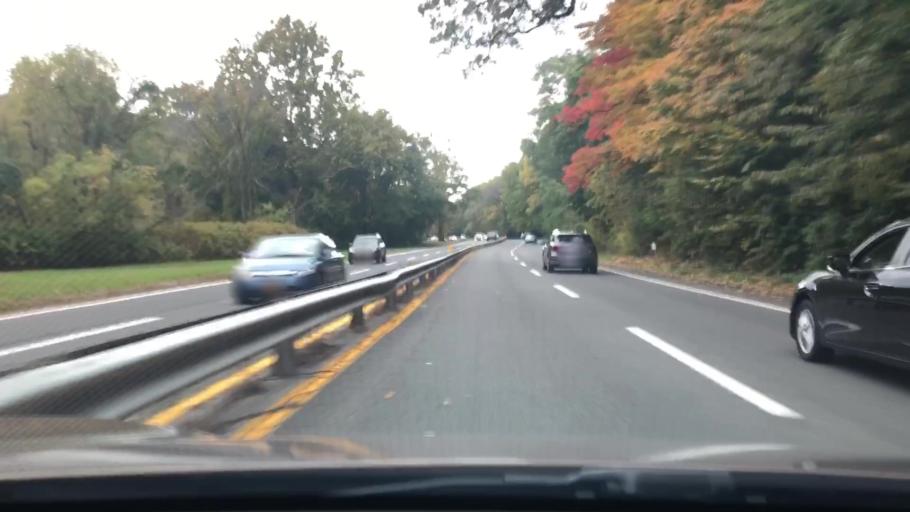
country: US
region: New York
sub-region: Westchester County
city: Tuckahoe
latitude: 40.9661
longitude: -73.8188
